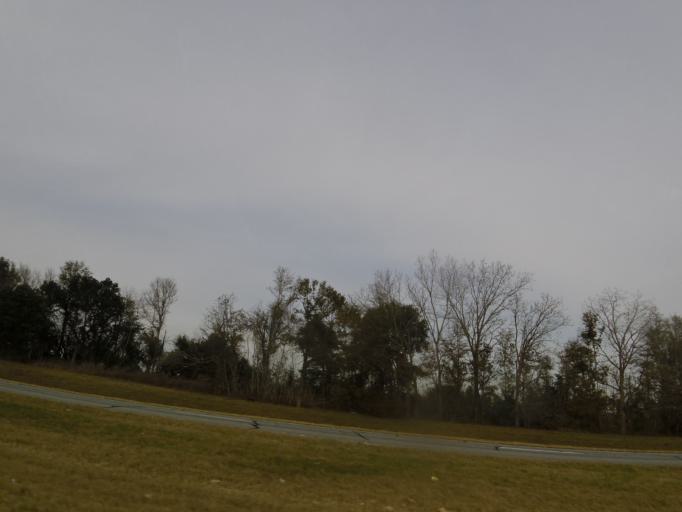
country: US
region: Georgia
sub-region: Seminole County
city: Donalsonville
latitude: 31.0028
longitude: -84.7886
